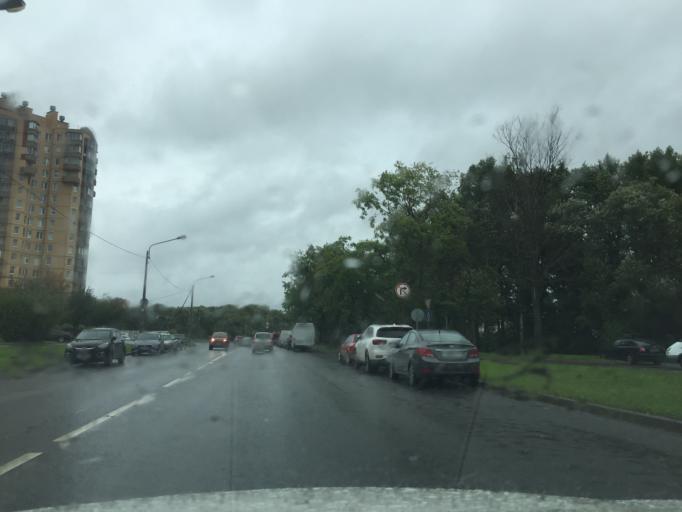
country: RU
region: St.-Petersburg
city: Uritsk
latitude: 59.8263
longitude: 30.1849
